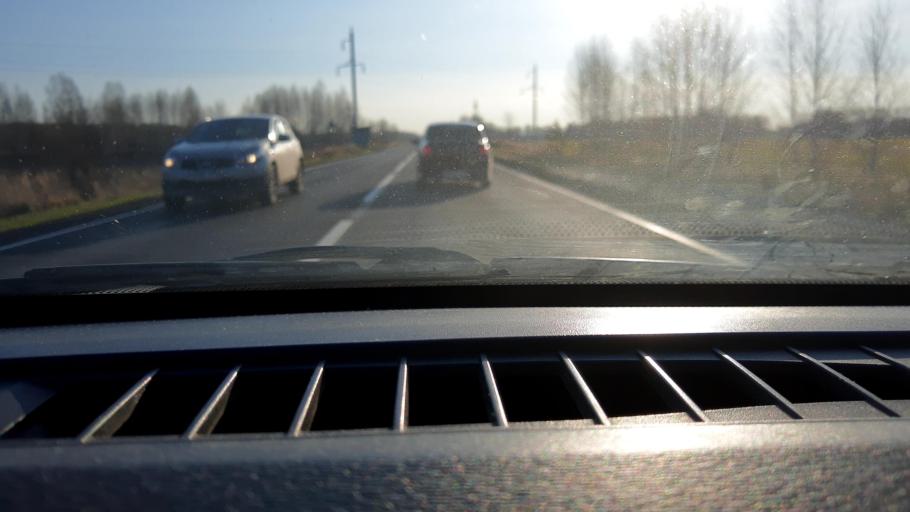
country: RU
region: Nizjnij Novgorod
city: Novaya Balakhna
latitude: 56.5888
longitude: 43.6664
